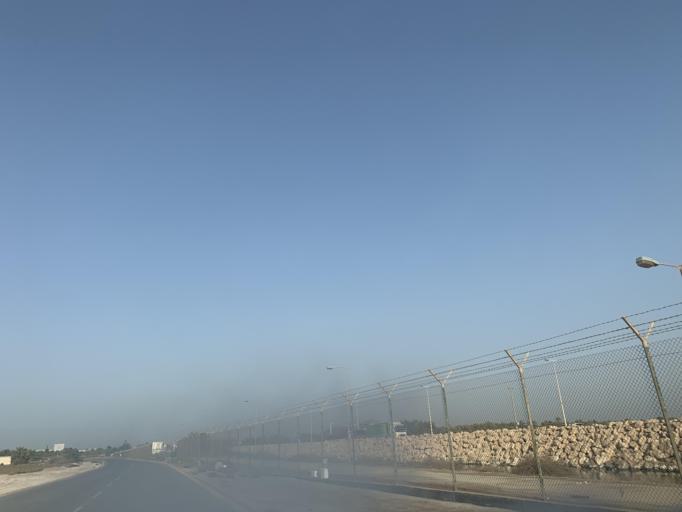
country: BH
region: Central Governorate
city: Madinat Hamad
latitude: 26.1723
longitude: 50.4485
